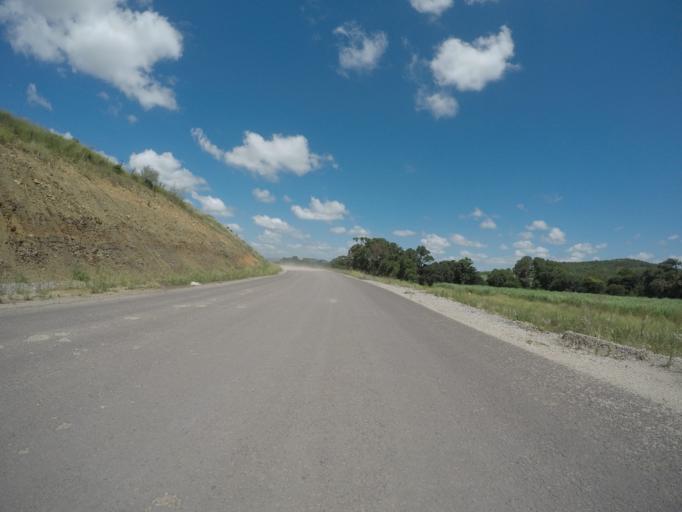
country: ZA
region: KwaZulu-Natal
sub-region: uThungulu District Municipality
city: Empangeni
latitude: -28.6544
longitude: 31.7690
